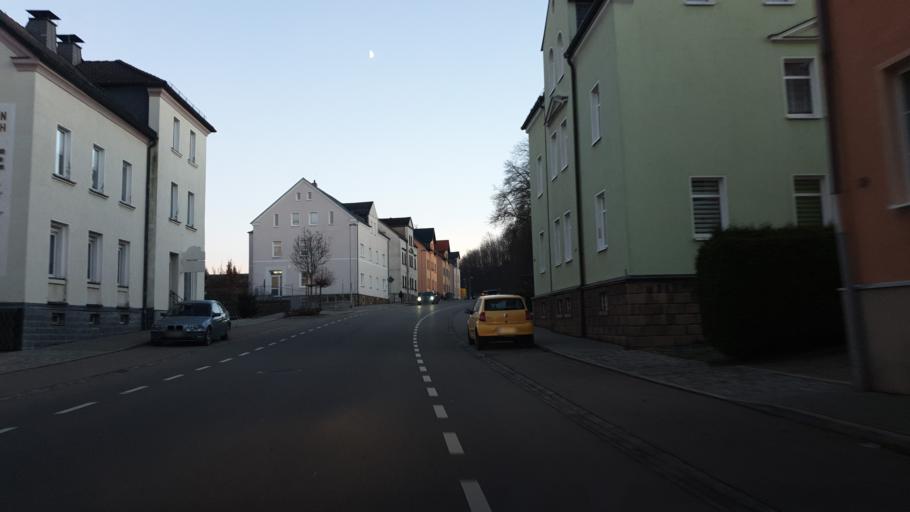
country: DE
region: Saxony
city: Hohndorf
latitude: 50.7397
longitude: 12.6815
